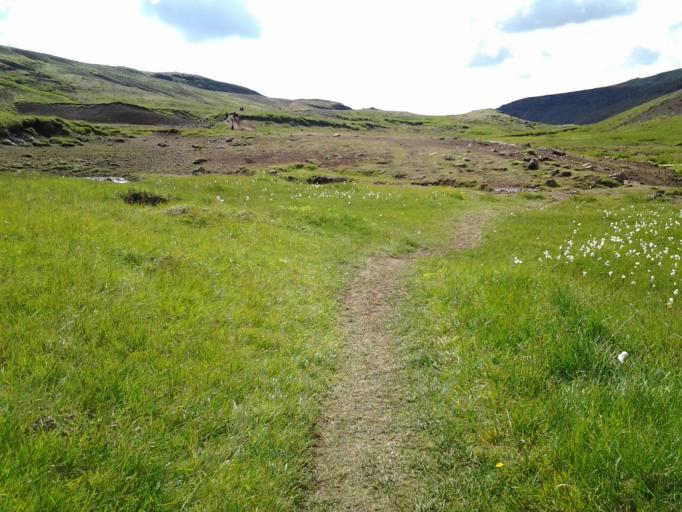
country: IS
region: South
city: Hveragerdi
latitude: 64.0406
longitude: -21.2186
